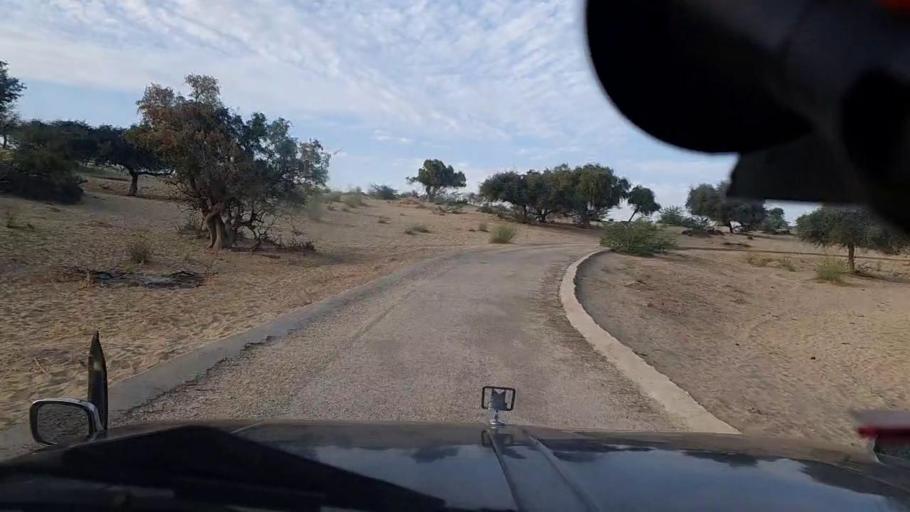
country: PK
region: Sindh
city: Diplo
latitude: 24.4688
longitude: 69.7901
